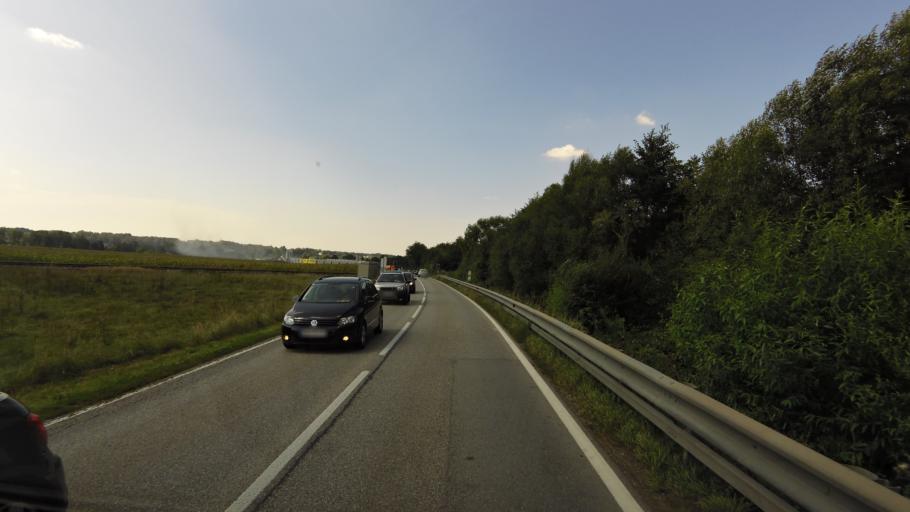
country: AT
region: Upper Austria
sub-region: Politischer Bezirk Braunau am Inn
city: Braunau am Inn
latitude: 48.1413
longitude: 13.1356
